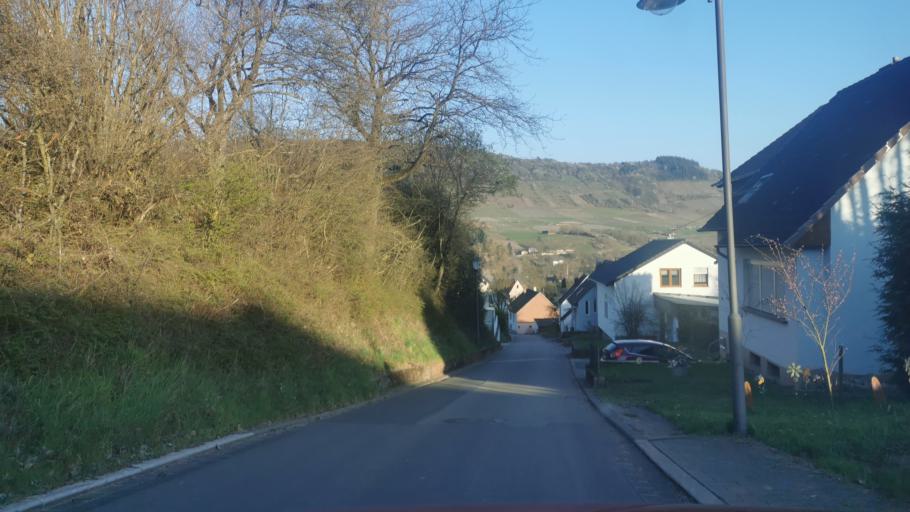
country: DE
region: Rheinland-Pfalz
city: Rivenich
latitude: 49.8768
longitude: 6.8409
